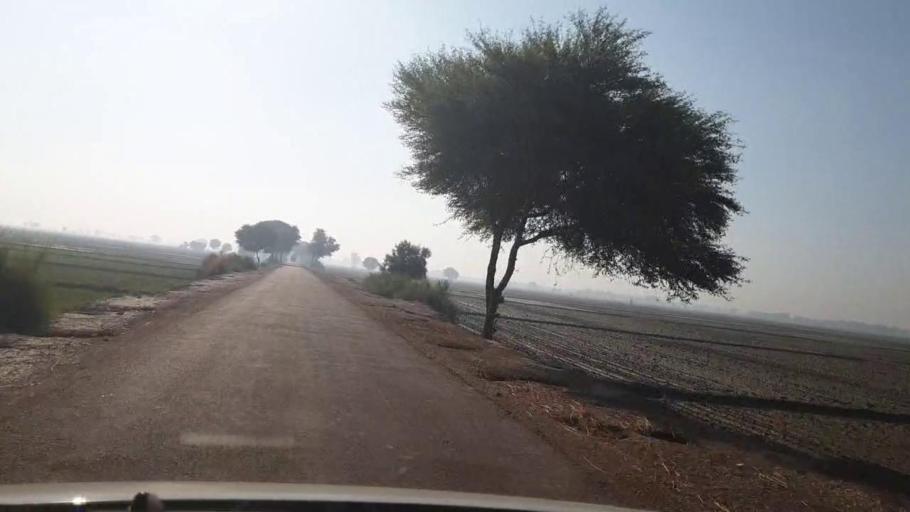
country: PK
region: Sindh
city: Dadu
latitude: 26.6687
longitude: 67.8156
